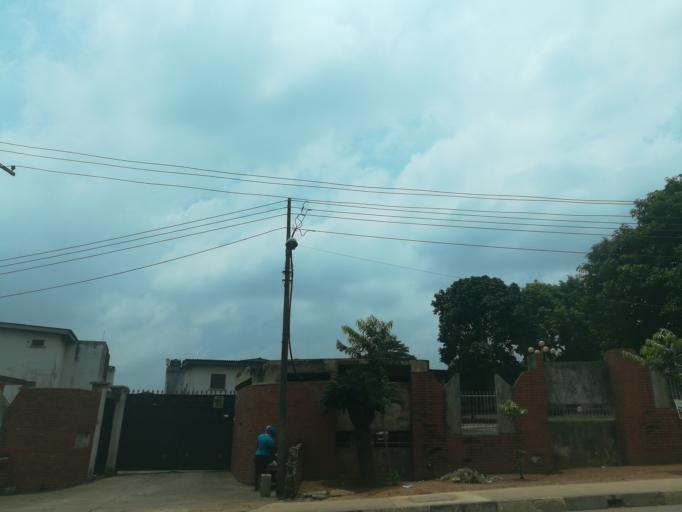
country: NG
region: Lagos
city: Ikorodu
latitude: 6.6235
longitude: 3.5233
